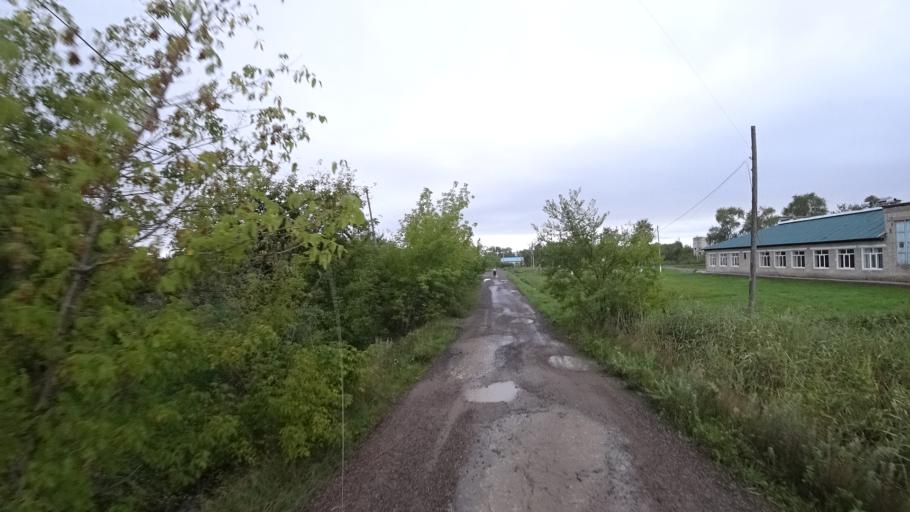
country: RU
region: Primorskiy
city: Chernigovka
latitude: 44.4058
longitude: 132.5319
